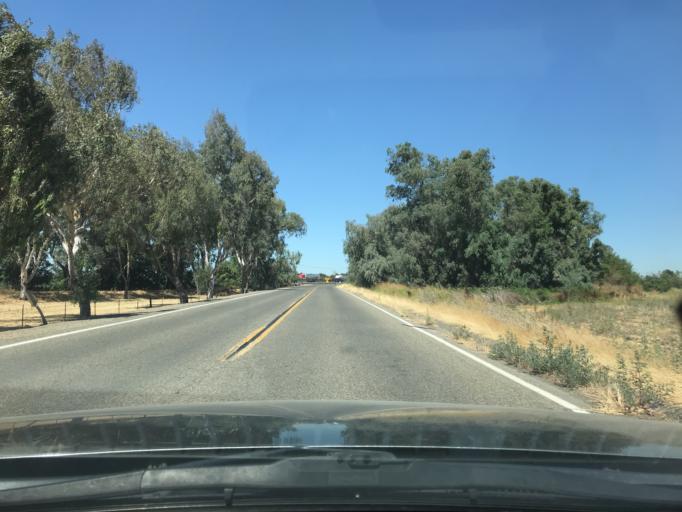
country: US
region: California
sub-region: Merced County
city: Merced
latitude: 37.3231
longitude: -120.5441
